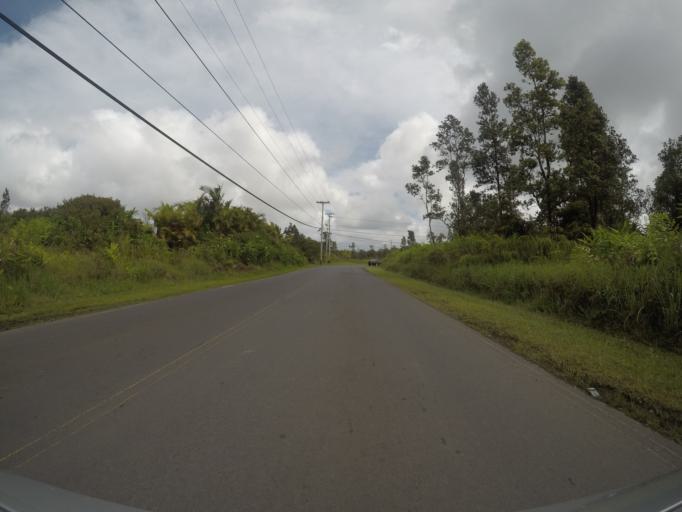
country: US
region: Hawaii
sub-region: Hawaii County
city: Fern Acres
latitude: 19.4783
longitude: -155.1420
